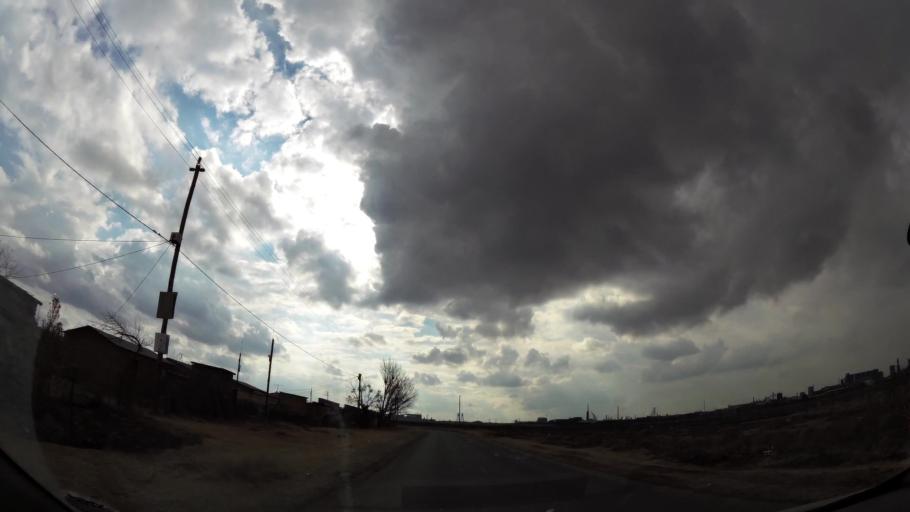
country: ZA
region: Orange Free State
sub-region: Fezile Dabi District Municipality
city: Sasolburg
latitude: -26.8406
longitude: 27.8645
